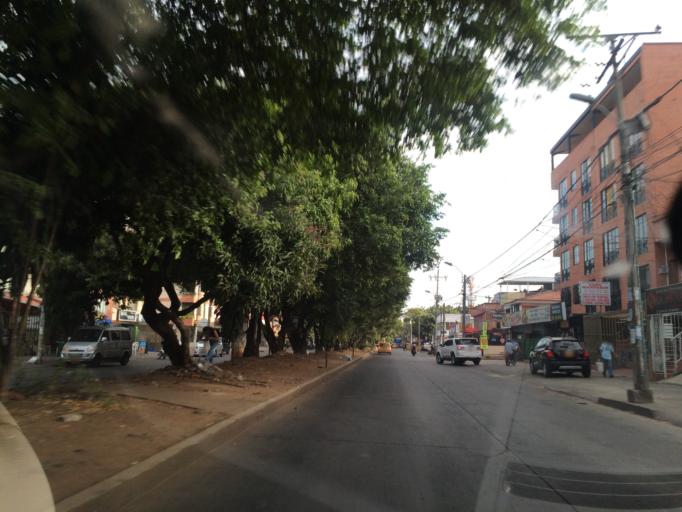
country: CO
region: Valle del Cauca
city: Cali
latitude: 3.4118
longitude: -76.5335
